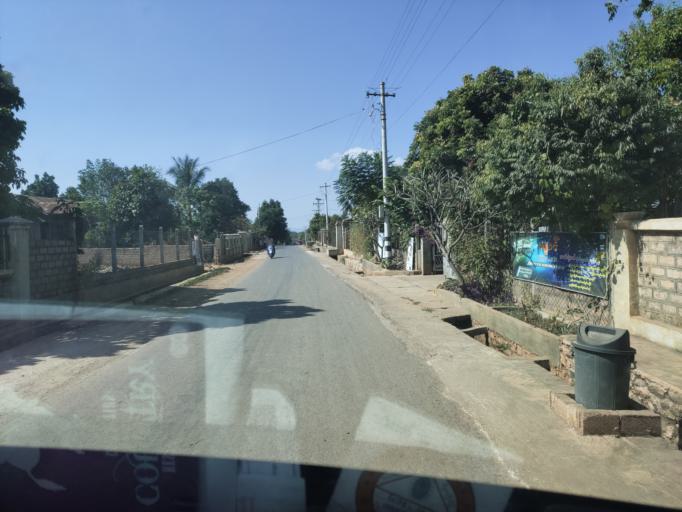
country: MM
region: Mandalay
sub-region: Pyin Oo Lwin District
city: Pyin Oo Lwin
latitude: 21.9534
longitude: 96.3935
